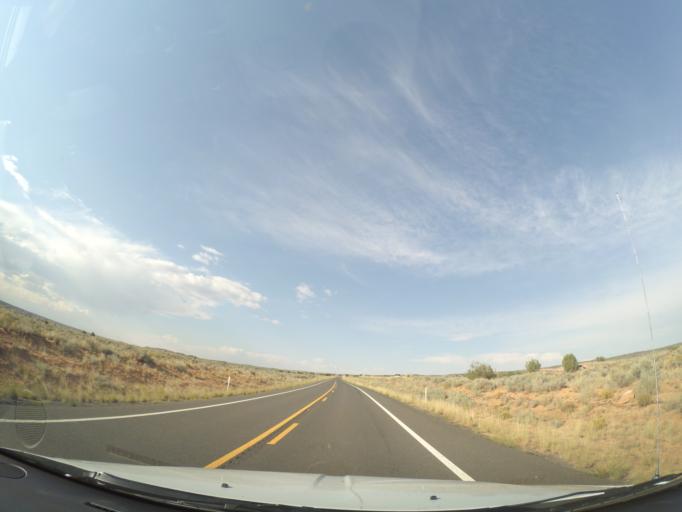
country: US
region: Arizona
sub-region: Coconino County
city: Kaibito
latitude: 36.4958
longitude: -111.4096
